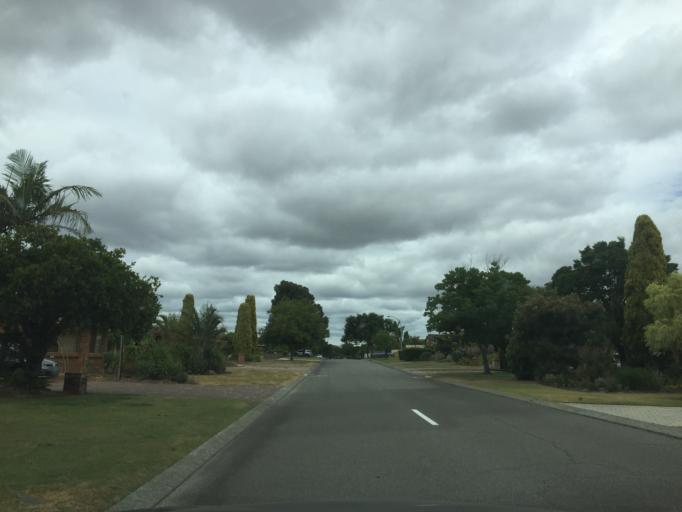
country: AU
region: Western Australia
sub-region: Gosnells
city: Thornlie
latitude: -32.0723
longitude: 115.9550
